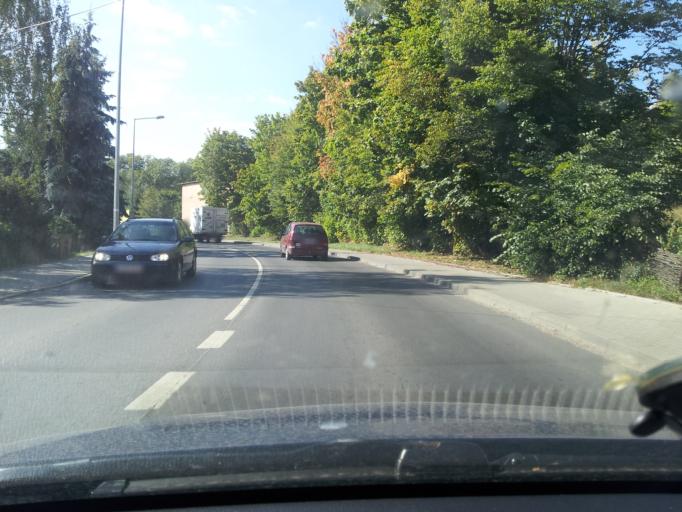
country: PL
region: Kujawsko-Pomorskie
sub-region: Powiat golubsko-dobrzynski
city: Golub-Dobrzyn
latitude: 53.1160
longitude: 19.0543
